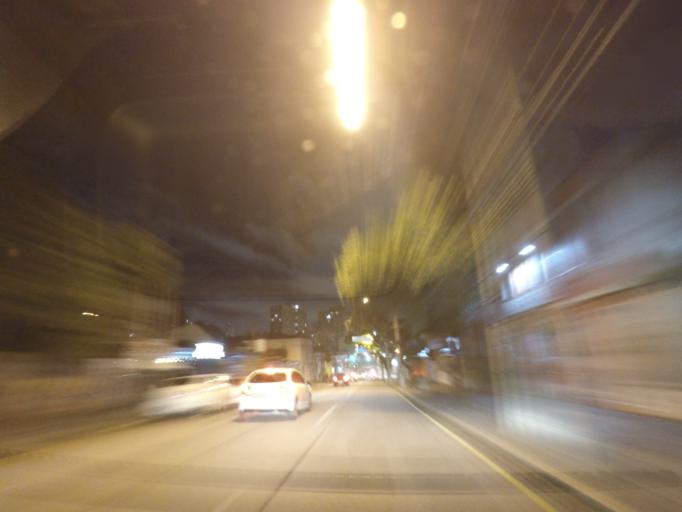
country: BR
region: Parana
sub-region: Curitiba
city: Curitiba
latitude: -25.4226
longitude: -49.2744
